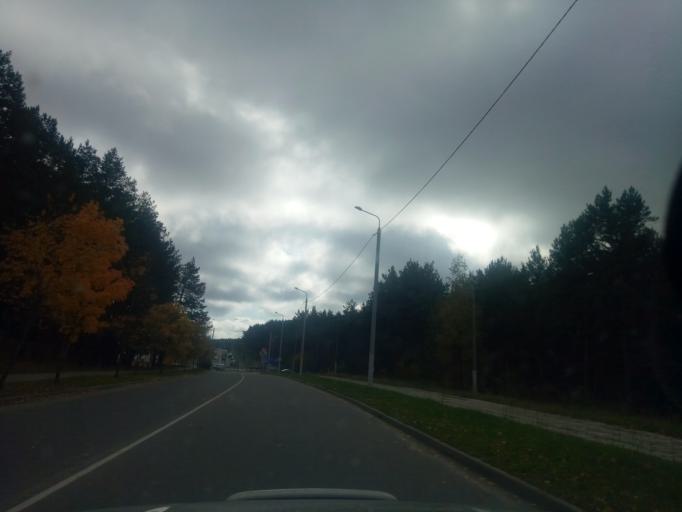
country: BY
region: Minsk
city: Zaslawye
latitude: 53.9934
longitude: 27.3002
